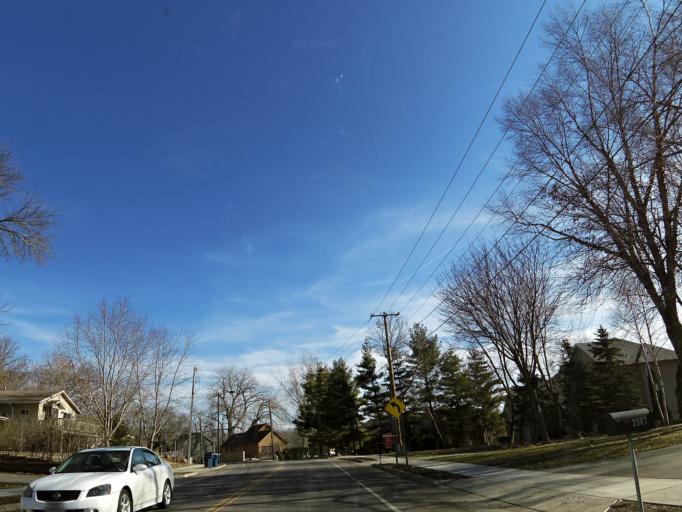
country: US
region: Minnesota
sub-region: Scott County
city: Prior Lake
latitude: 44.7037
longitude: -93.4602
